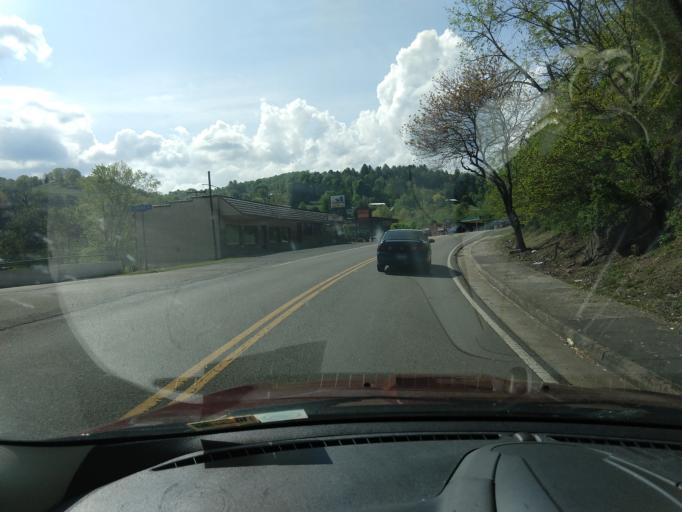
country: US
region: Virginia
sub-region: Russell County
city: Honaker
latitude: 37.0156
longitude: -81.9702
